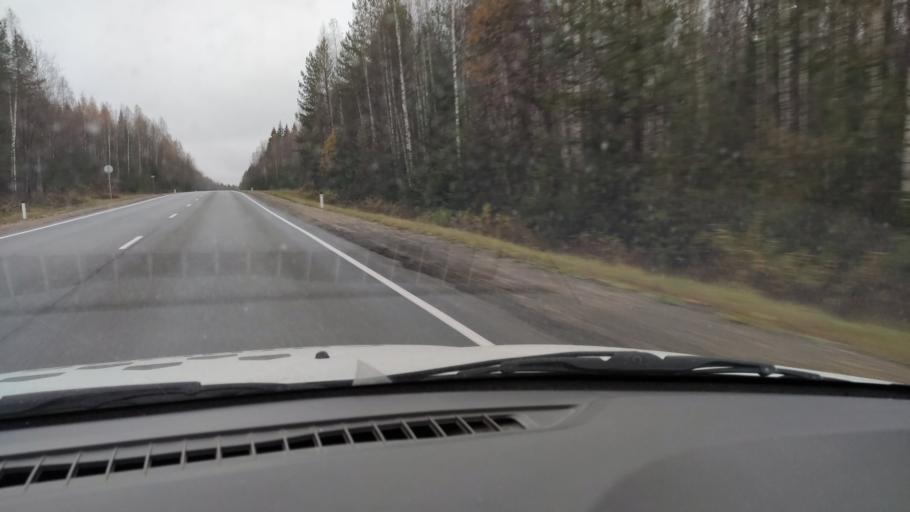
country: RU
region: Kirov
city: Chernaya Kholunitsa
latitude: 58.7735
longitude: 51.9412
